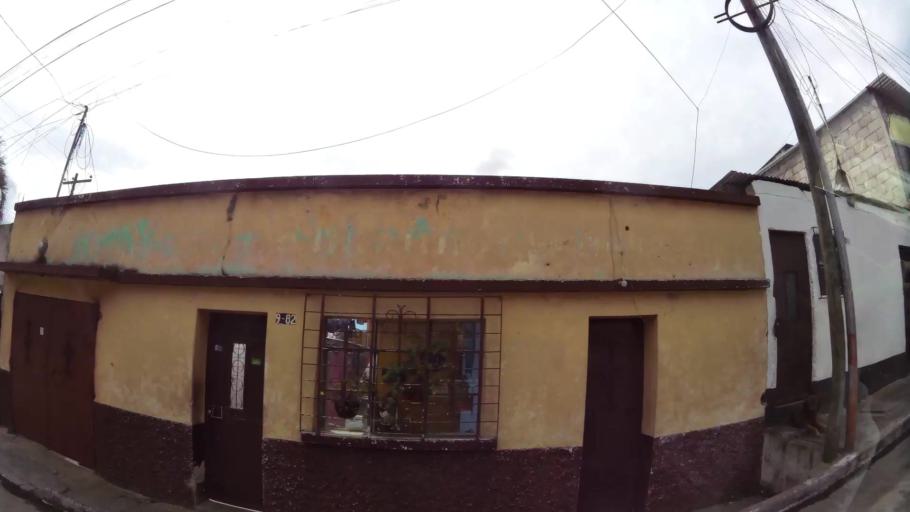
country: GT
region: Guatemala
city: Santa Catarina Pinula
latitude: 14.5665
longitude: -90.5367
